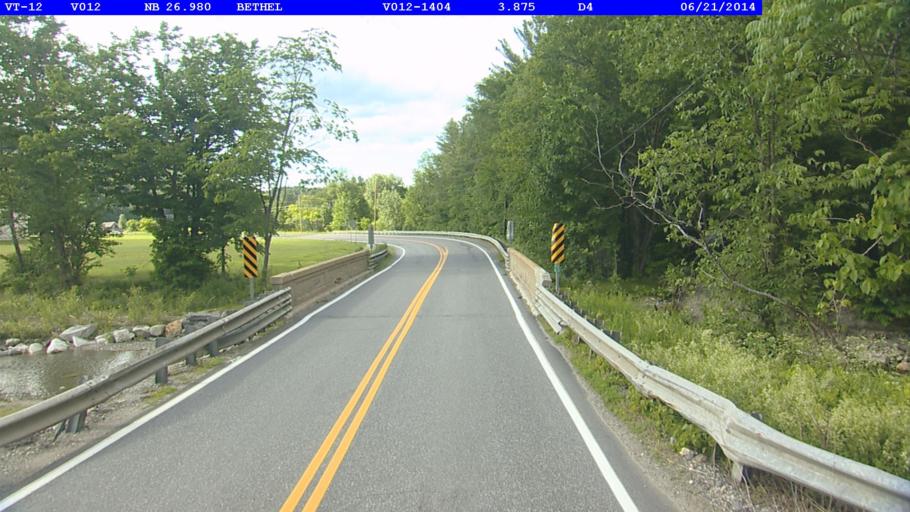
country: US
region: Vermont
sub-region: Orange County
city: Randolph
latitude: 43.8535
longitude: -72.6469
